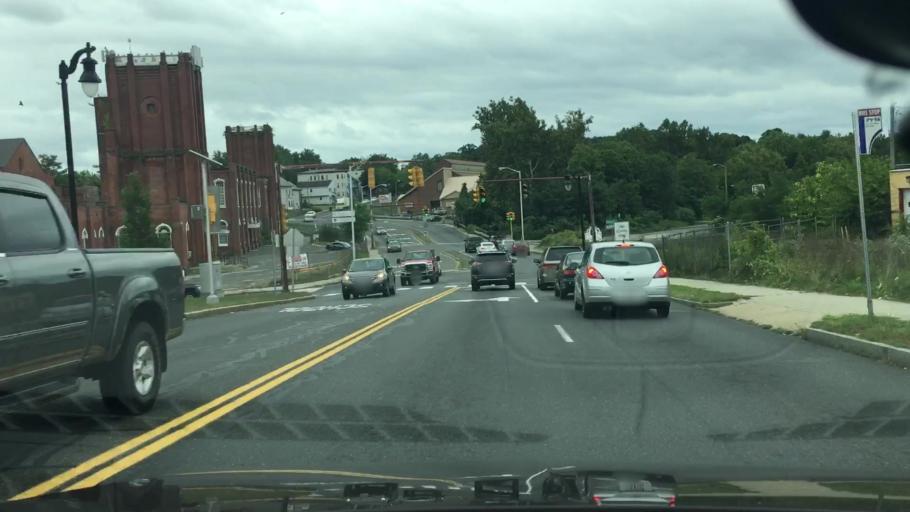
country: US
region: Massachusetts
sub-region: Hampden County
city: Springfield
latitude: 42.0984
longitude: -72.5642
